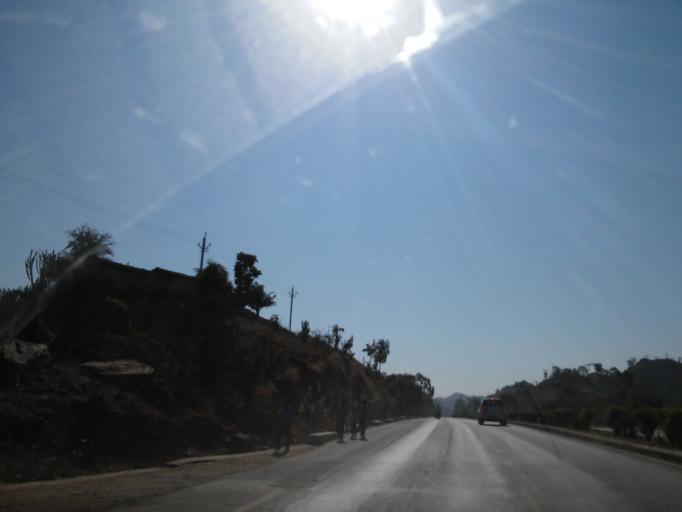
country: IN
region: Rajasthan
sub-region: Udaipur
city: Udaipur
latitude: 24.2403
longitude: 73.6792
